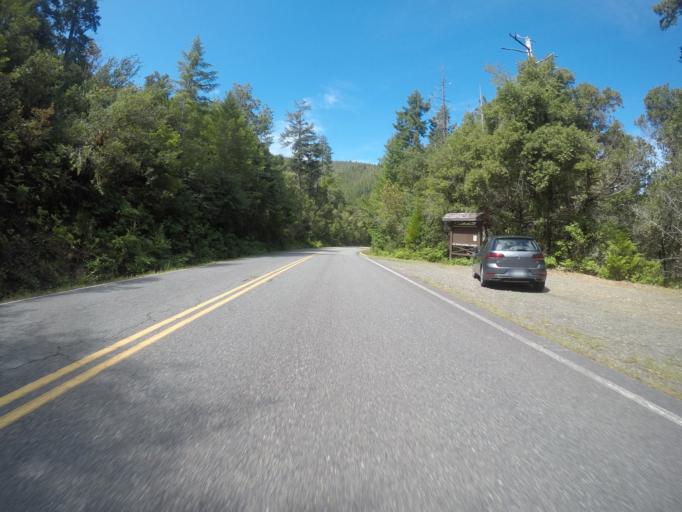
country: US
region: California
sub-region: Del Norte County
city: Bertsch-Oceanview
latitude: 41.7249
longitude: -123.9680
